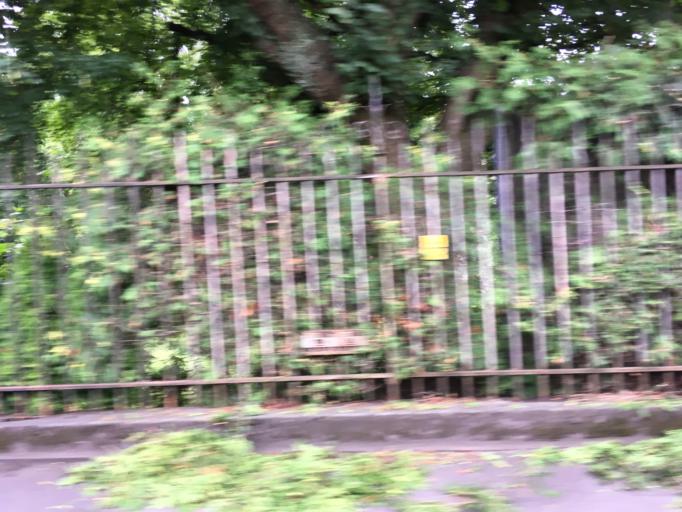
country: CH
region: Bern
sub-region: Thun District
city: Hilterfingen
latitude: 46.7437
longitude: 7.6477
